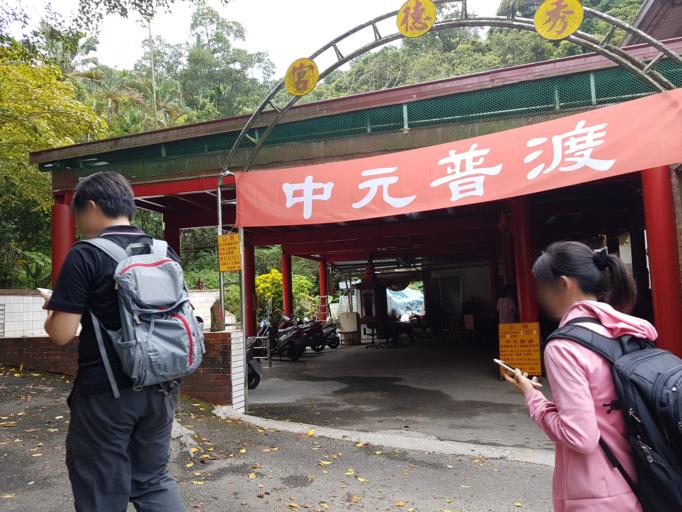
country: TW
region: Taiwan
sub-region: Keelung
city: Keelung
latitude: 25.0578
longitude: 121.6623
